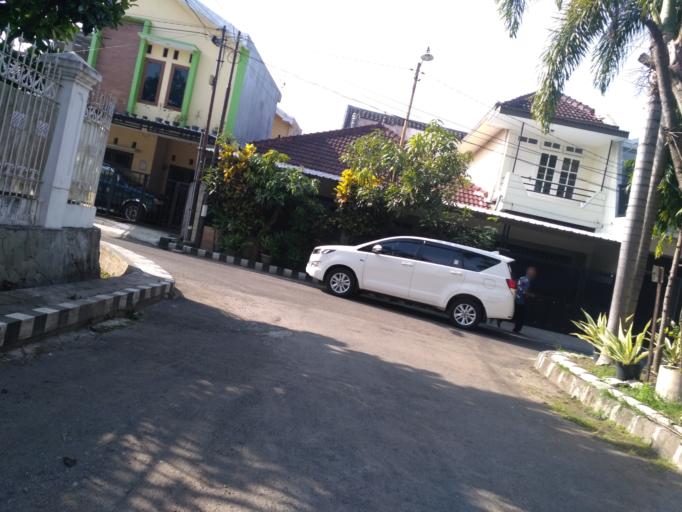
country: ID
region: East Java
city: Malang
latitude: -7.9476
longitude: 112.6226
